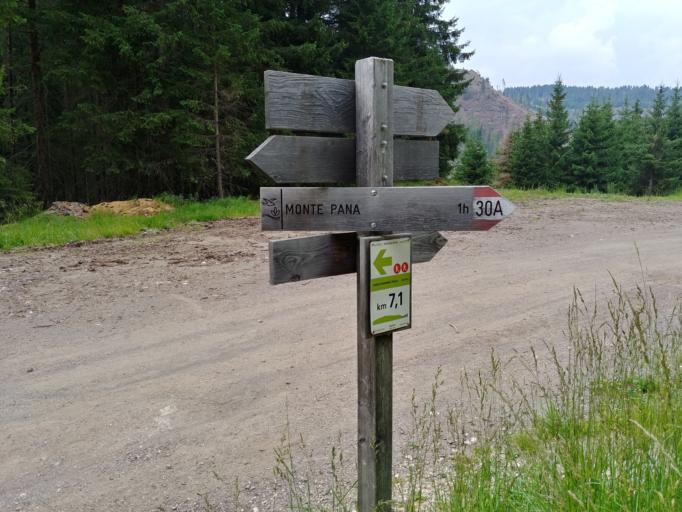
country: IT
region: Trentino-Alto Adige
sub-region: Bolzano
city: Ortisei
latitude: 46.5374
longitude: 11.6894
